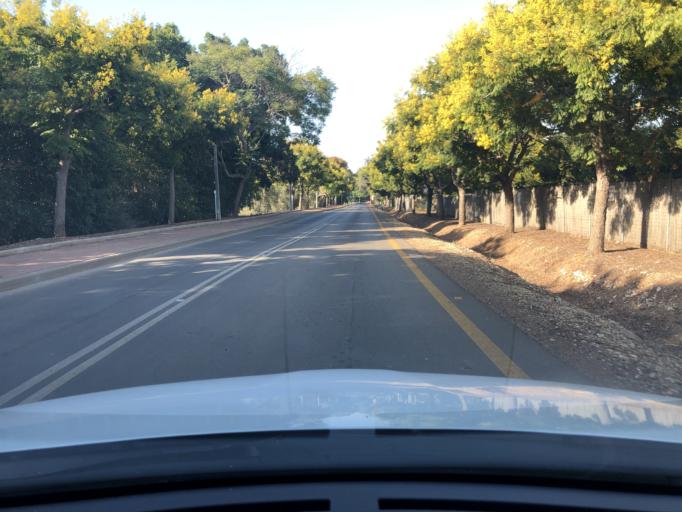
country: IL
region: Central District
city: Hod HaSharon
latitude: 32.1366
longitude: 34.9075
